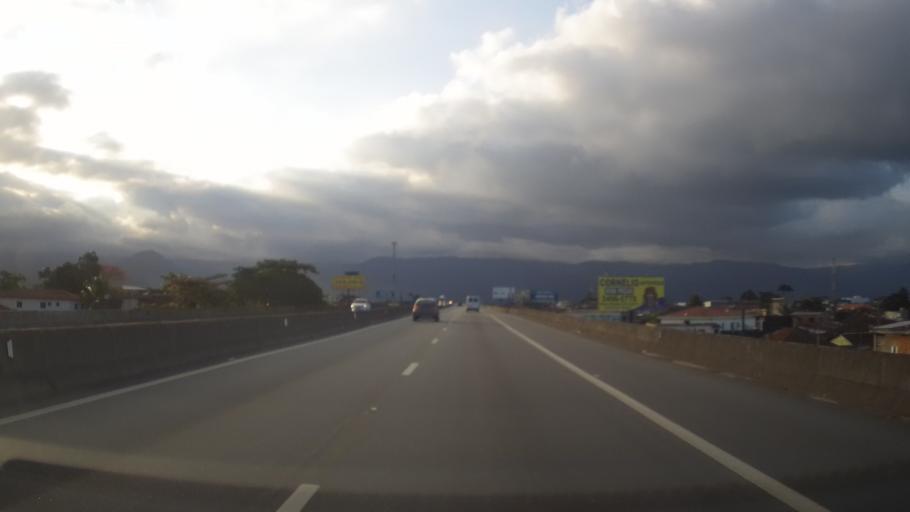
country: BR
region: Sao Paulo
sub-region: Sao Vicente
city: Sao Vicente
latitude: -23.9640
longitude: -46.4020
